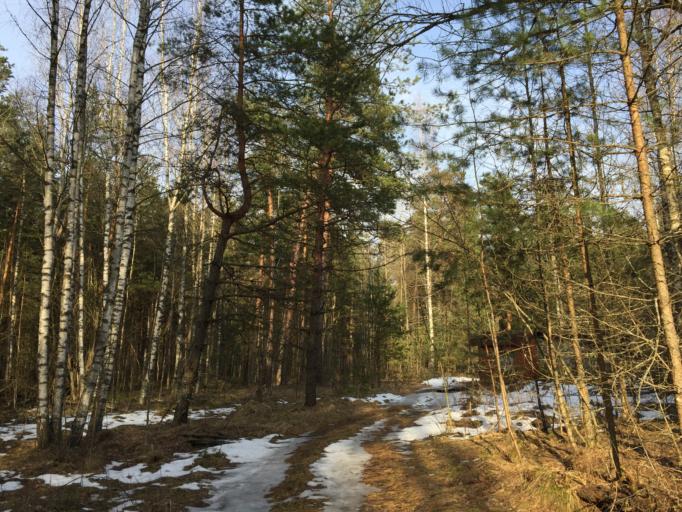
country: LV
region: Stopini
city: Ulbroka
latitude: 56.9498
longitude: 24.2957
